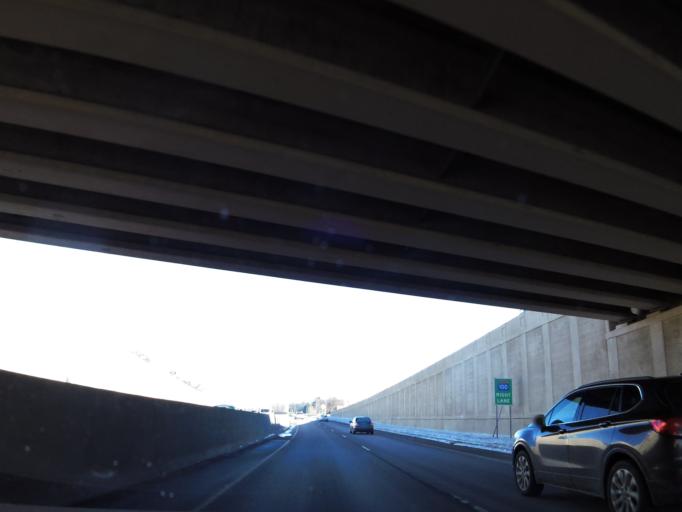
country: US
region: Minnesota
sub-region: Hennepin County
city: Saint Louis Park
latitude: 44.9390
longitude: -93.3567
